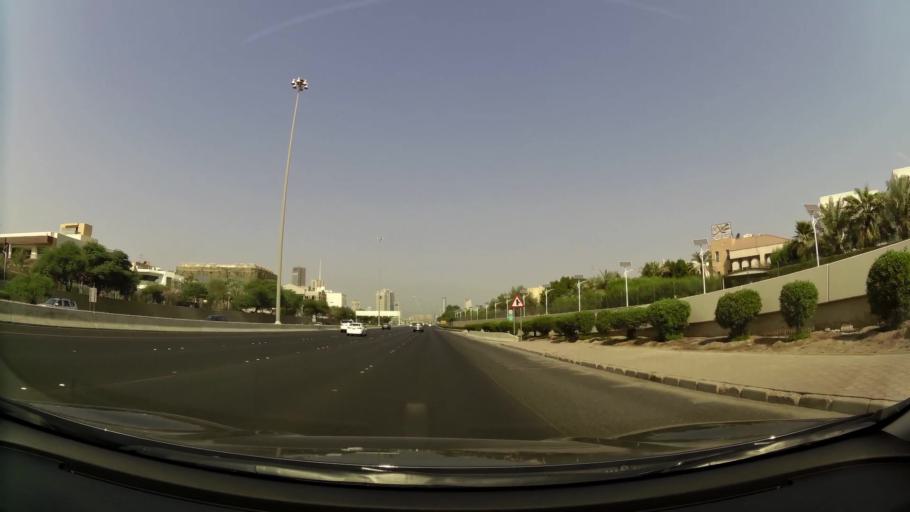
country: KW
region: Al Asimah
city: Ad Dasmah
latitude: 29.3518
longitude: 47.9932
